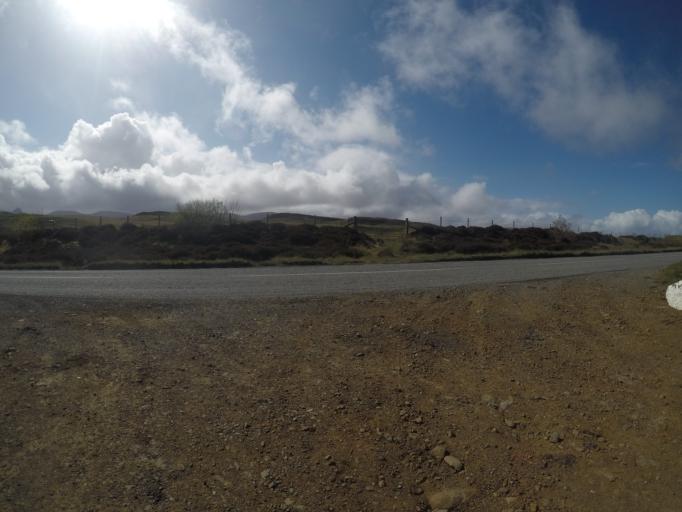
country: GB
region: Scotland
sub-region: Highland
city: Portree
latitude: 57.5868
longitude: -6.1570
